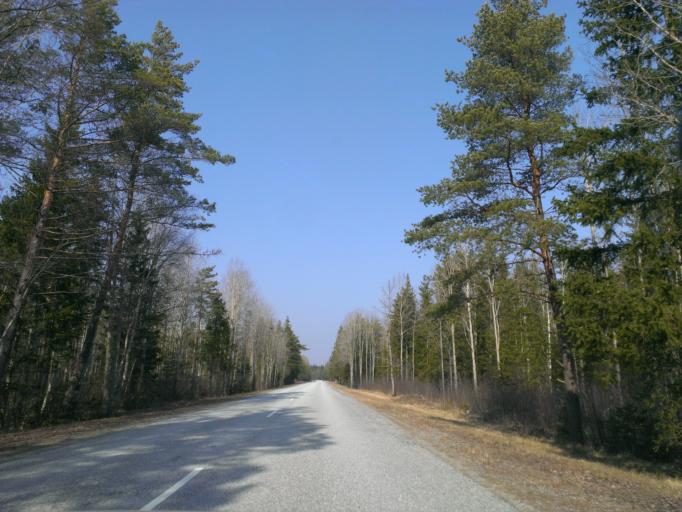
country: EE
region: Saare
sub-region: Kuressaare linn
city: Kuressaare
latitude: 58.3526
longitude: 22.6760
